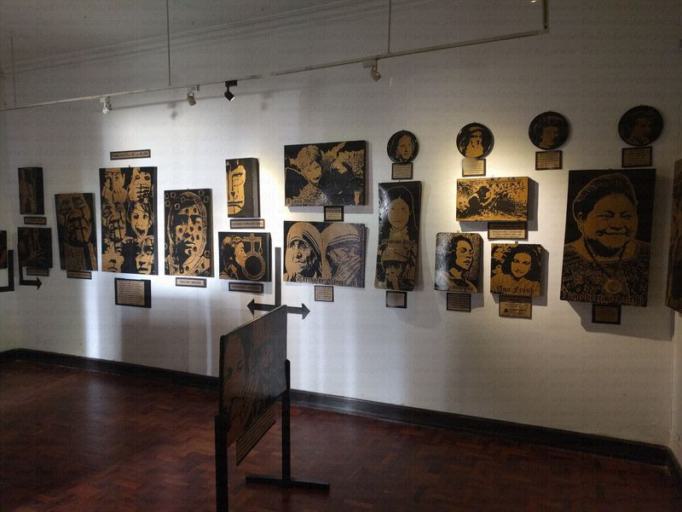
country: BO
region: Chuquisaca
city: Sucre
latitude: -19.0475
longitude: -65.2598
